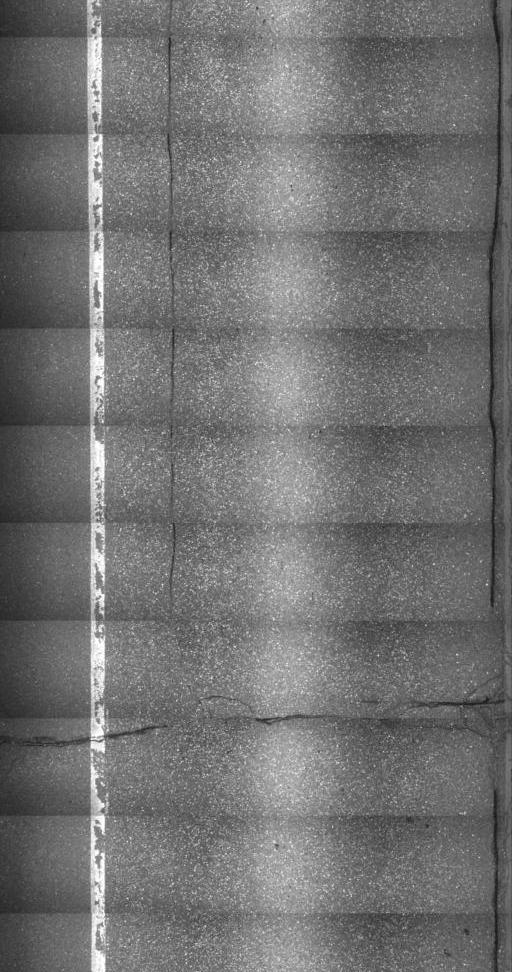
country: US
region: Vermont
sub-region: Chittenden County
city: Williston
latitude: 44.4402
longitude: -73.0812
